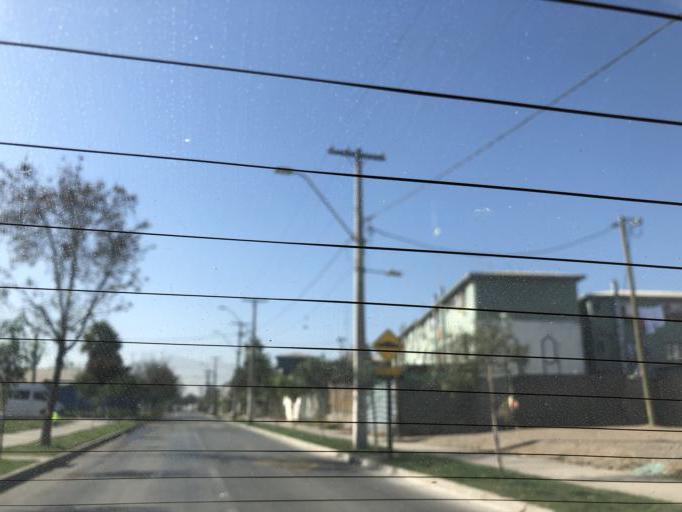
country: CL
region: Santiago Metropolitan
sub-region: Provincia de Santiago
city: La Pintana
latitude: -33.6291
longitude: -70.6276
